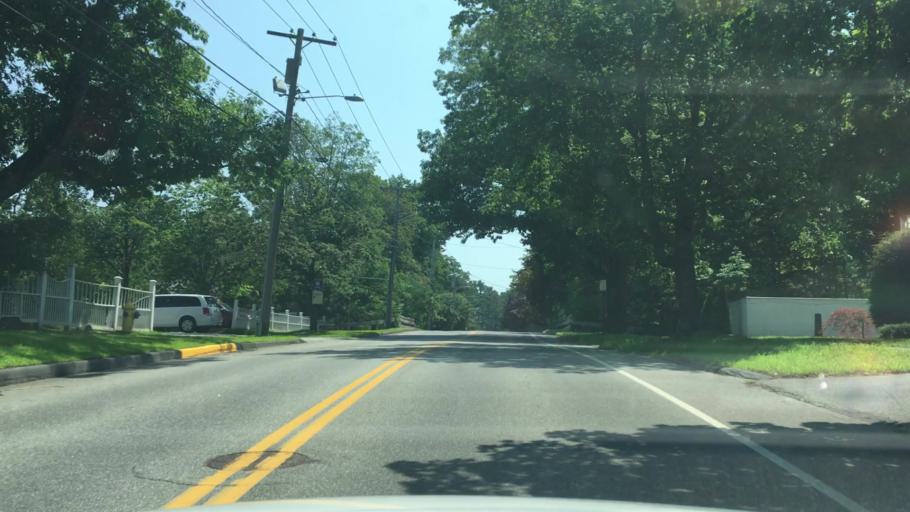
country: US
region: Maine
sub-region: Cumberland County
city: Brunswick
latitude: 43.9129
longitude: -69.9612
